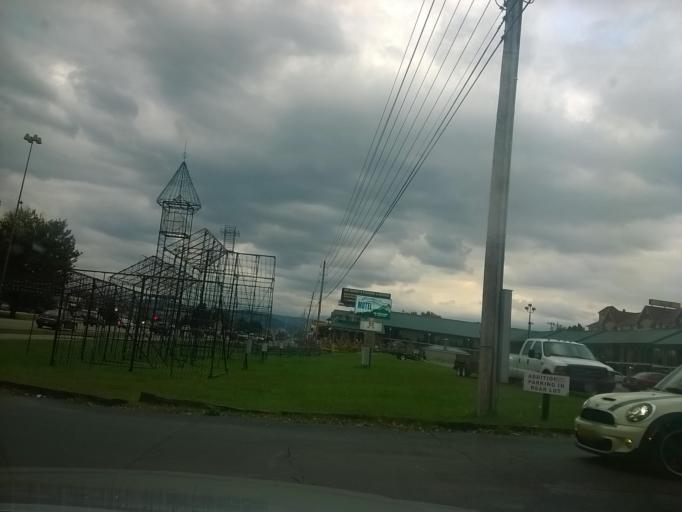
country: US
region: Tennessee
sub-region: Sevier County
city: Pigeon Forge
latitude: 35.7967
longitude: -83.5661
